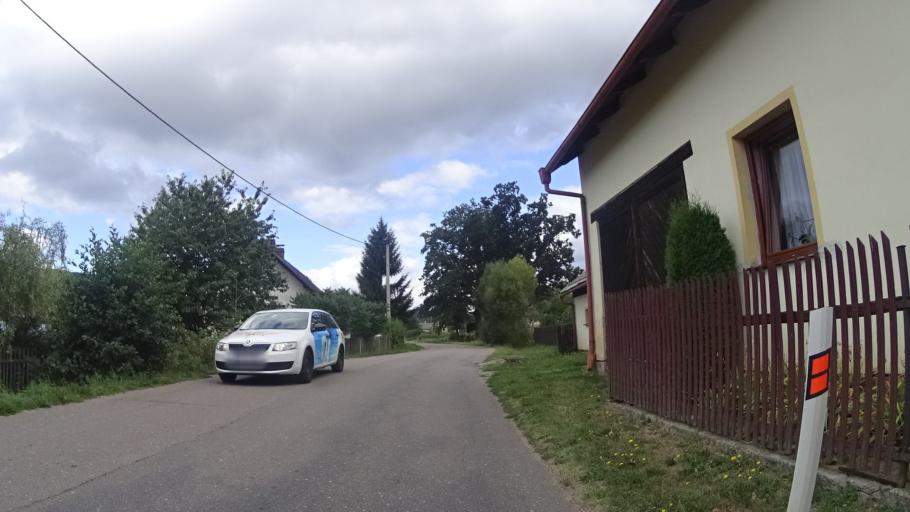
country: CZ
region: Pardubicky
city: Dolni Cermna
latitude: 49.9358
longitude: 16.5319
